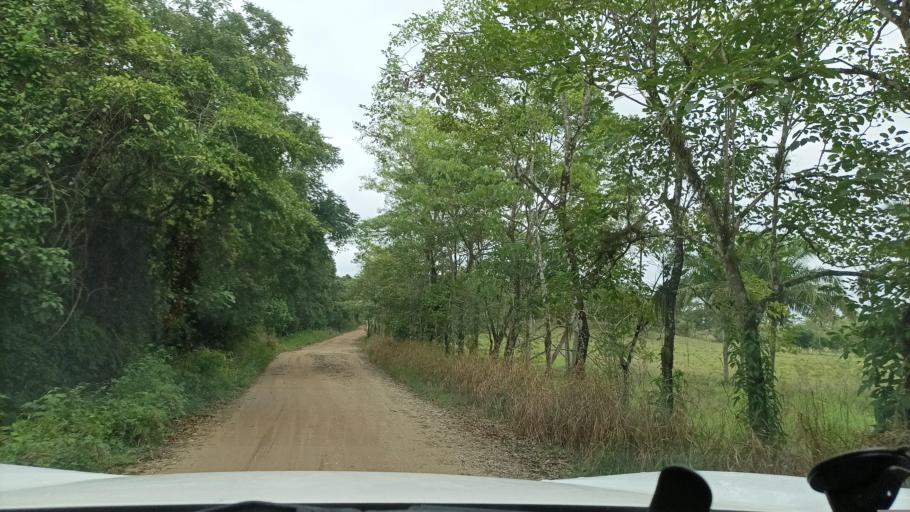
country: MX
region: Veracruz
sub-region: Moloacan
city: Cuichapa
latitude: 17.7899
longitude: -94.3664
